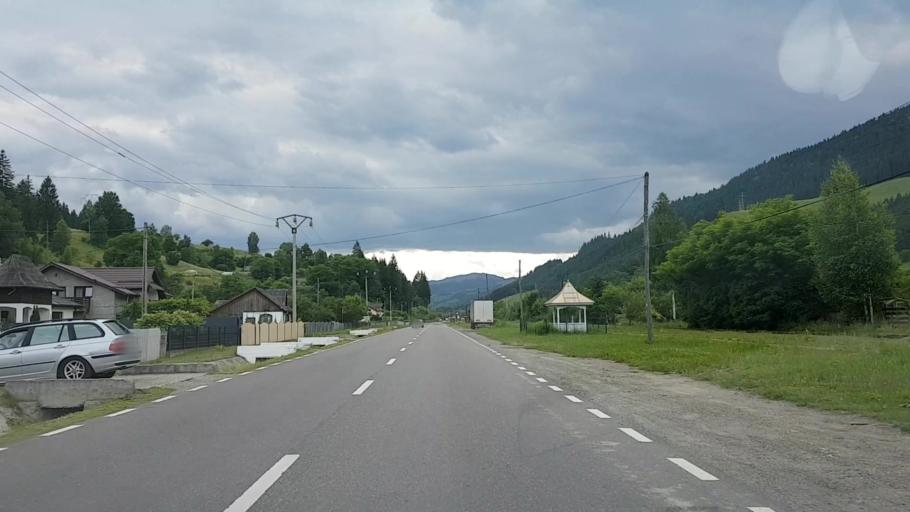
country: RO
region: Neamt
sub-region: Comuna Tasca
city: Tasca
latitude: 46.8890
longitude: 26.0133
